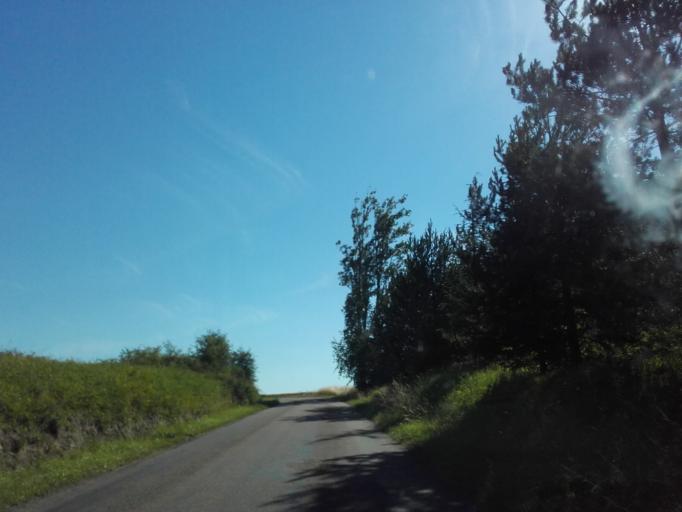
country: FR
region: Bourgogne
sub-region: Departement de Saone-et-Loire
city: Saint-Leger-sur-Dheune
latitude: 46.8791
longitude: 4.6377
